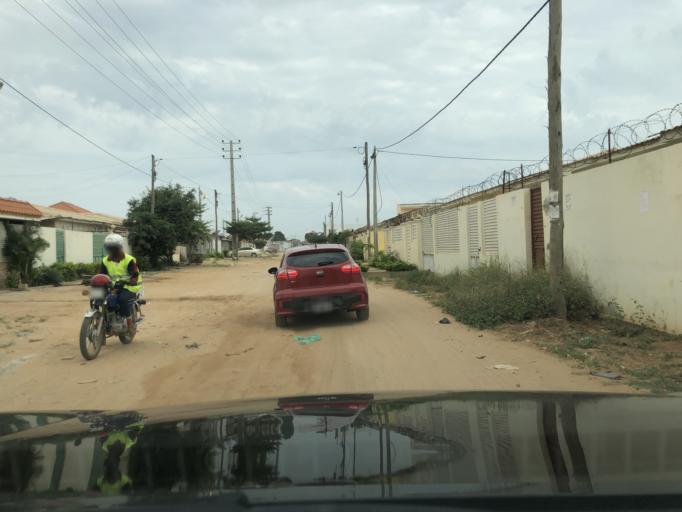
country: AO
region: Luanda
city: Luanda
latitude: -8.9370
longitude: 13.2421
